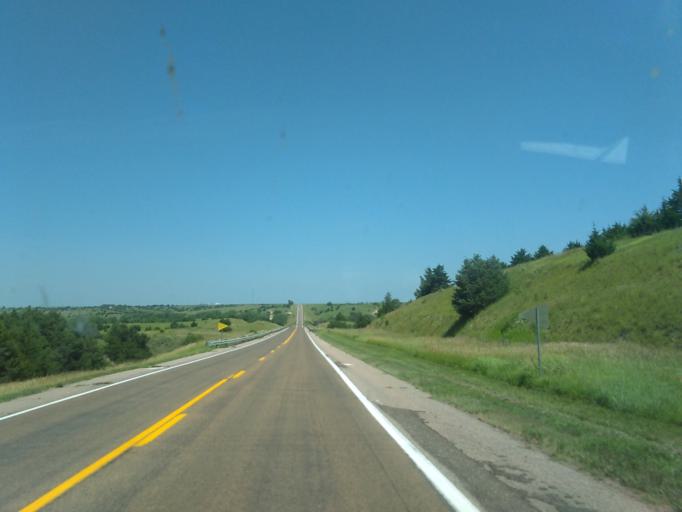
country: US
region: Nebraska
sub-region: Frontier County
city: Stockville
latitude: 40.6222
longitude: -100.6306
